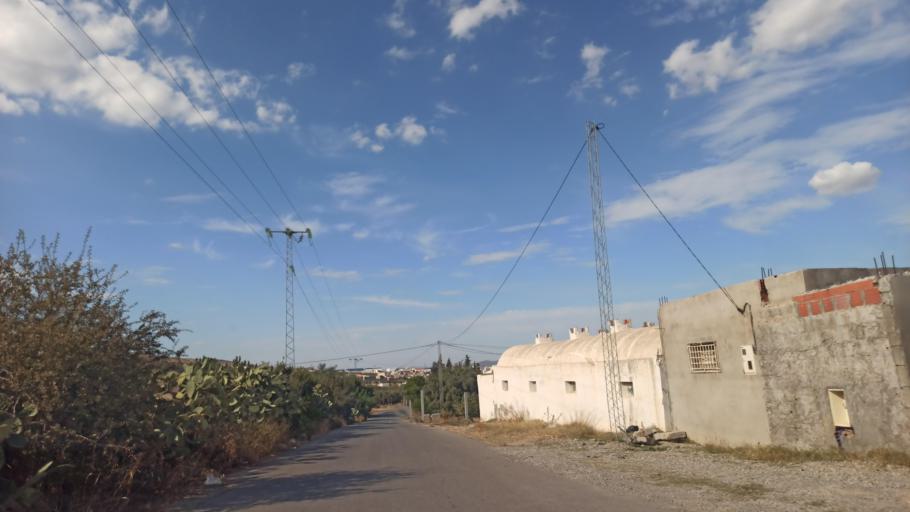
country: TN
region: Zaghwan
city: Zaghouan
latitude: 36.3375
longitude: 10.2103
